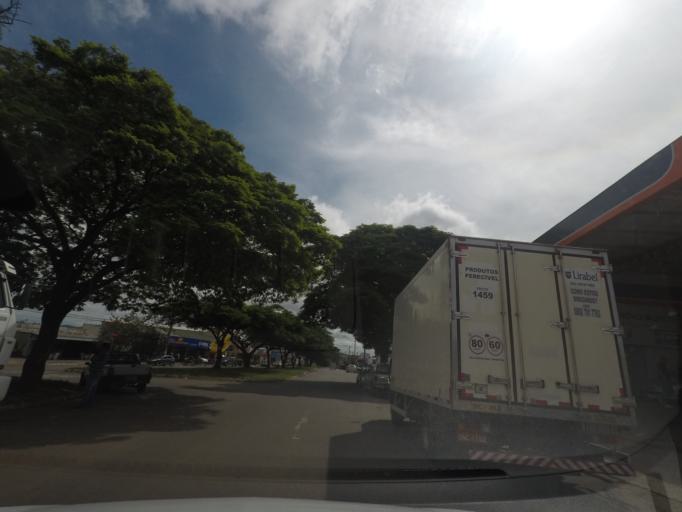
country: BR
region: Goias
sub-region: Goiania
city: Goiania
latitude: -16.6690
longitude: -49.2198
